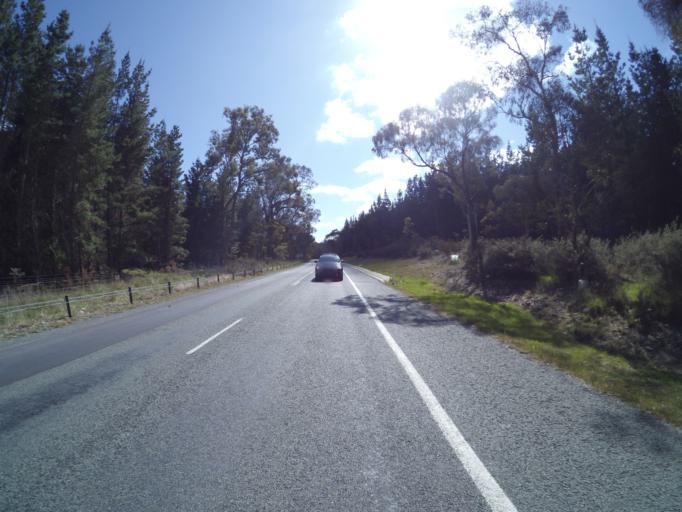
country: AU
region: New South Wales
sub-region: Queanbeyan
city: Queanbeyan
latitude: -35.2724
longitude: 149.2600
